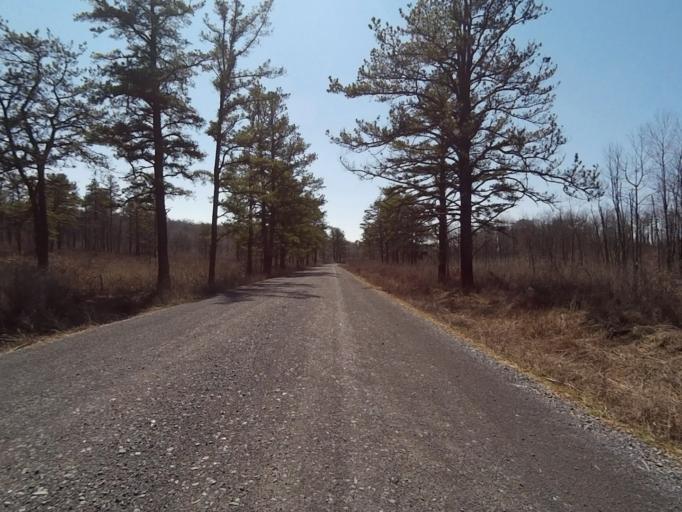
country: US
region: Pennsylvania
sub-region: Centre County
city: Park Forest Village
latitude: 40.7792
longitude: -77.9534
